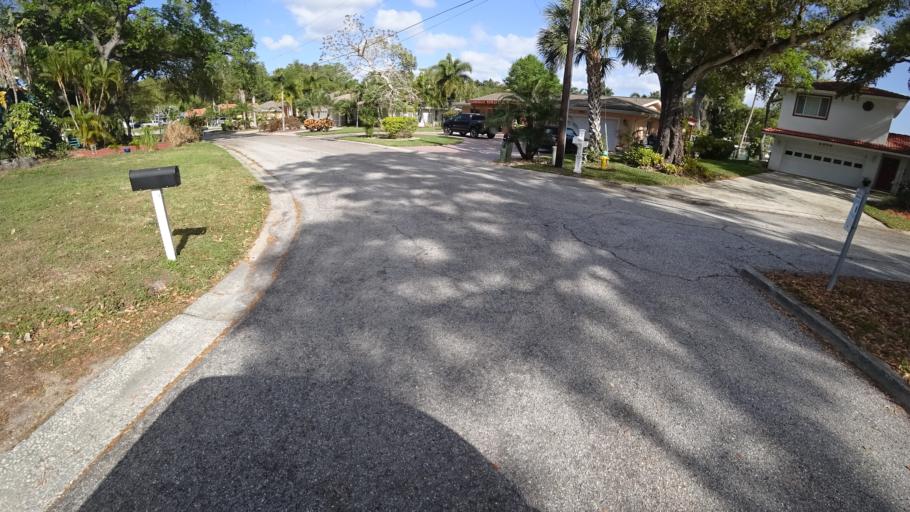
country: US
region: Florida
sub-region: Manatee County
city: Whitfield
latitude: 27.4178
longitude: -82.5668
